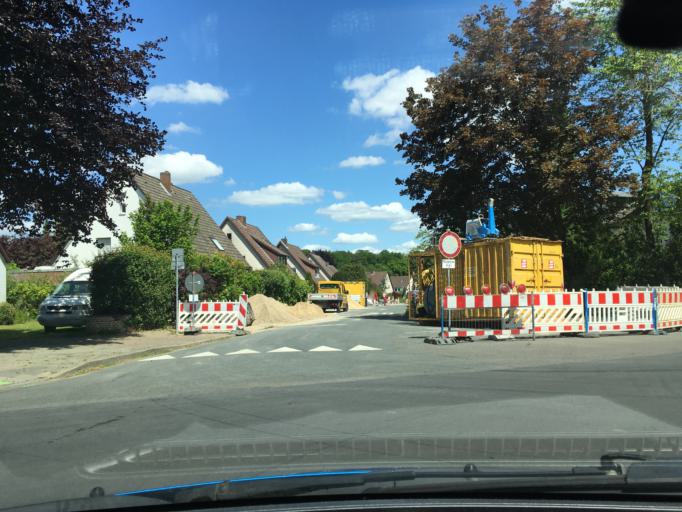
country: DE
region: Lower Saxony
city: Uelzen
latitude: 52.9713
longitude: 10.5337
